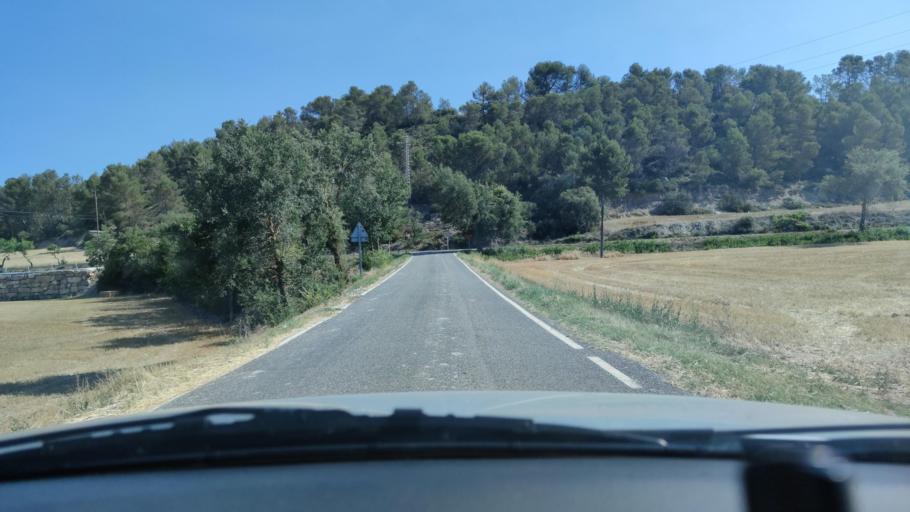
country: ES
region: Catalonia
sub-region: Provincia de Lleida
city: Sant Guim de Freixenet
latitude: 41.6662
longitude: 1.3694
